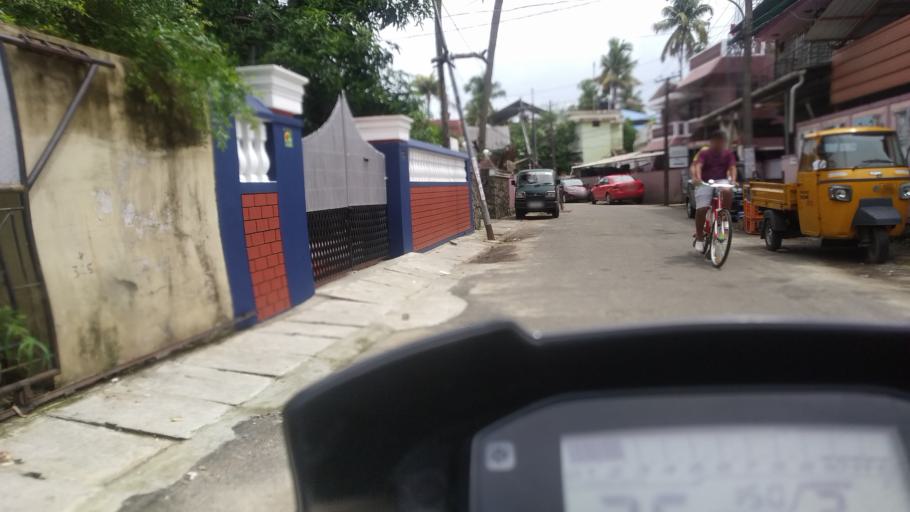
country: IN
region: Kerala
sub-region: Ernakulam
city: Elur
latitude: 10.0060
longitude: 76.2833
